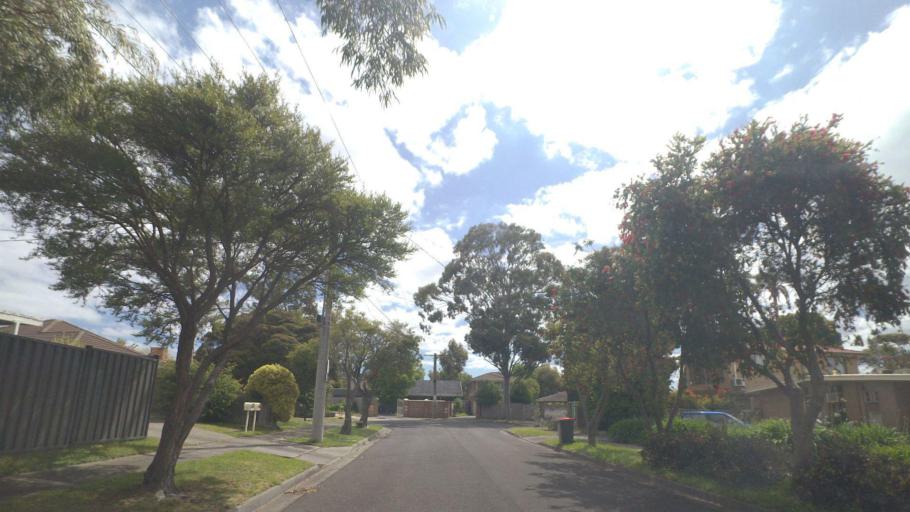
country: AU
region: Victoria
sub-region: Knox
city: Knoxfield
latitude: -37.8721
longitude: 145.2390
